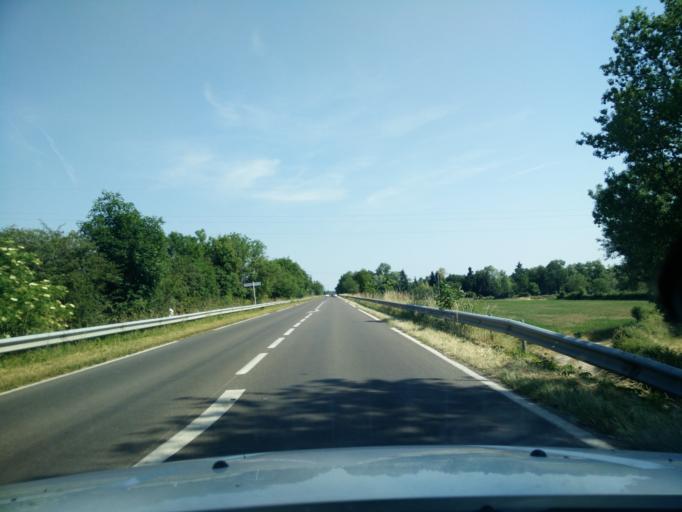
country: FR
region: Auvergne
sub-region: Departement de l'Allier
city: Moulins
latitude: 46.5319
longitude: 3.3189
